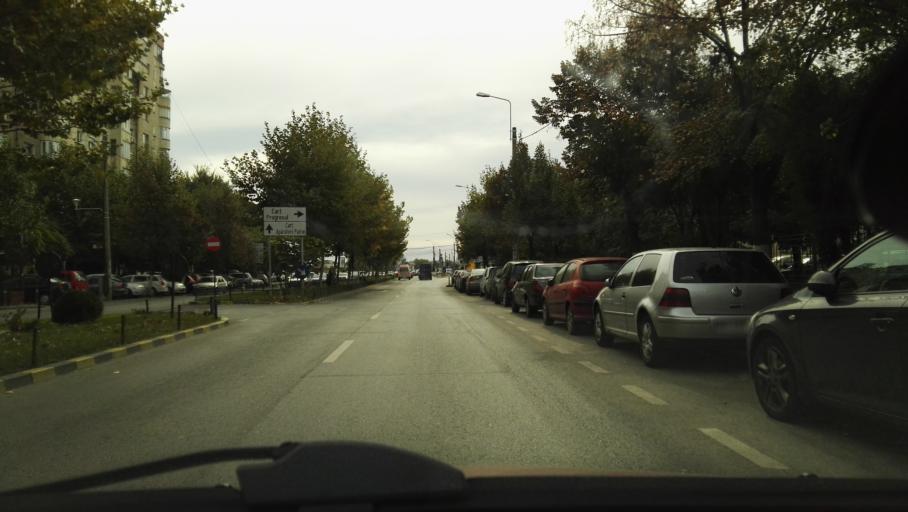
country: RO
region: Ilfov
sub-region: Comuna Popesti-Leordeni
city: Popesti-Leordeni
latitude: 44.3812
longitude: 26.1333
